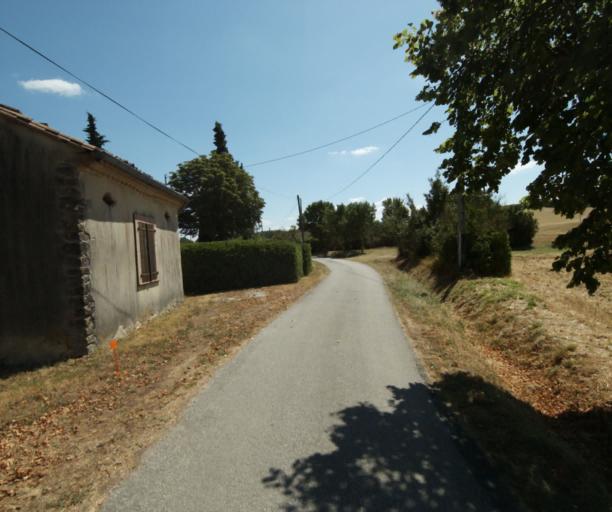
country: FR
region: Midi-Pyrenees
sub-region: Departement de la Haute-Garonne
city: Saint-Felix-Lauragais
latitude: 43.4761
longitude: 1.8796
